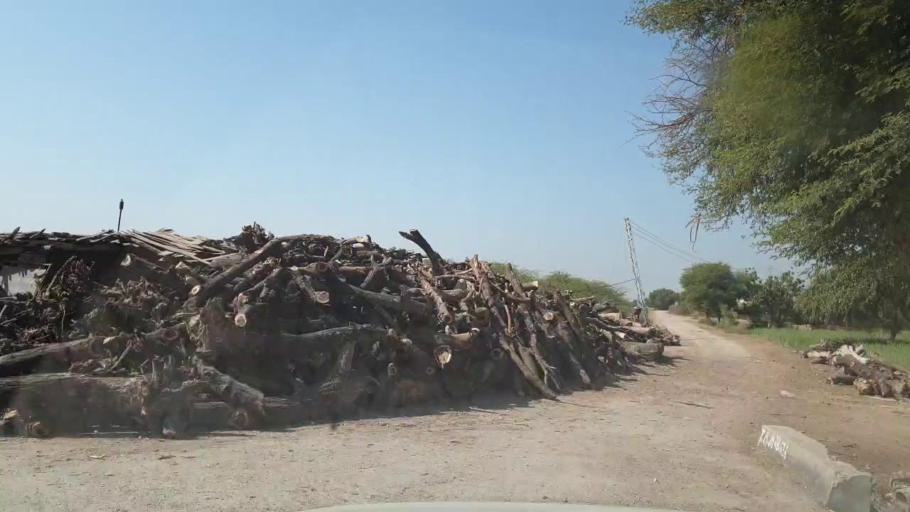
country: PK
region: Sindh
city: Mirpur Khas
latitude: 25.6311
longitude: 69.0923
